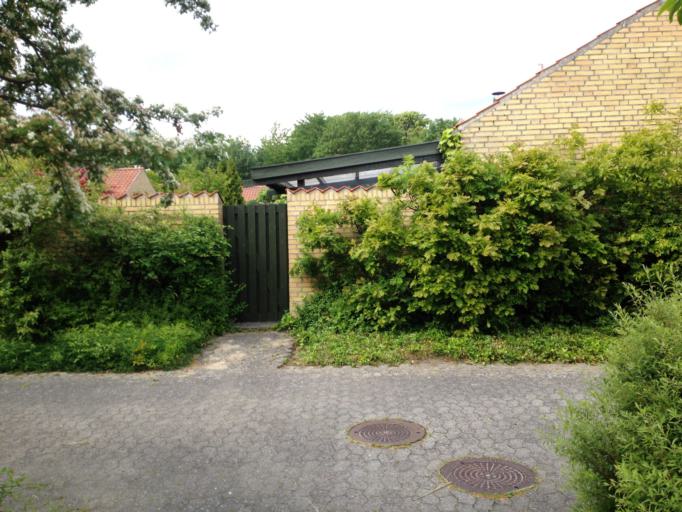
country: DK
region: Capital Region
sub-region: Fredensborg Kommune
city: Niva
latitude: 55.9322
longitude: 12.5010
